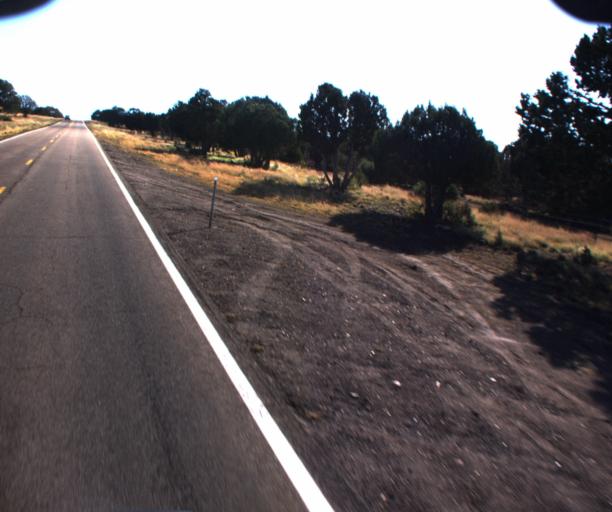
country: US
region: Arizona
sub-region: Navajo County
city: White Mountain Lake
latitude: 34.2888
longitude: -109.8202
